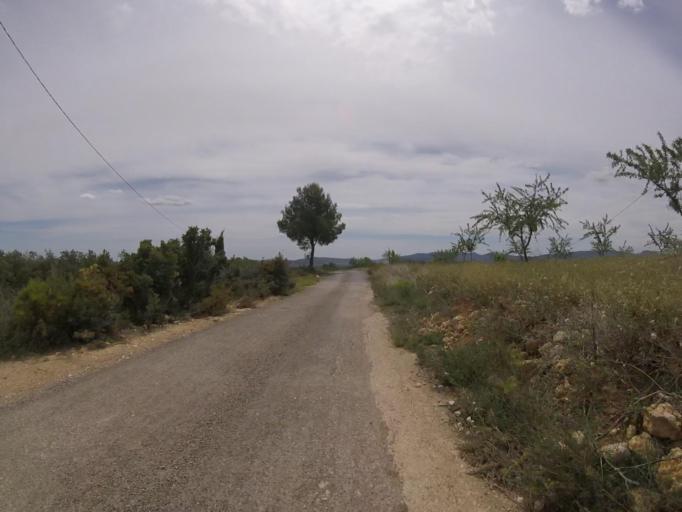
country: ES
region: Valencia
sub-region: Provincia de Castello
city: Benlloch
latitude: 40.2206
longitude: -0.0190
